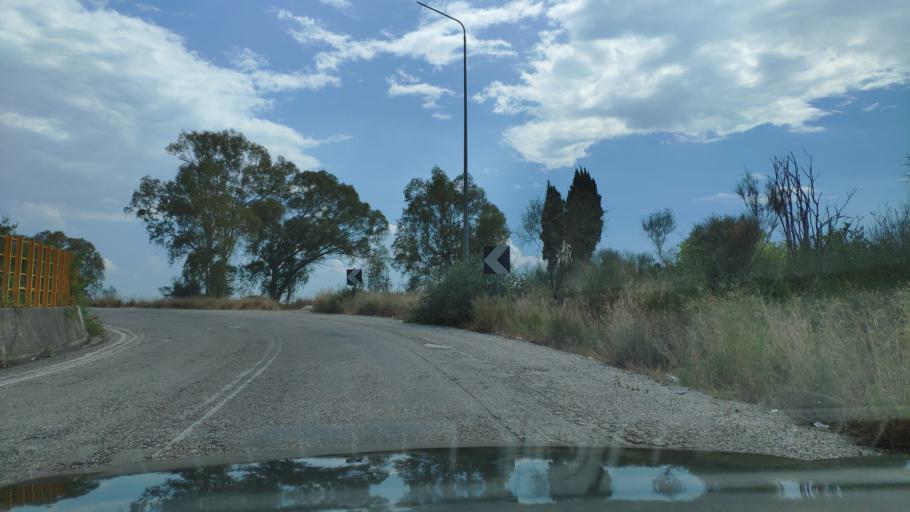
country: GR
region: West Greece
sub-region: Nomos Aitolias kai Akarnanias
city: Menidi
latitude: 39.0210
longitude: 21.1346
